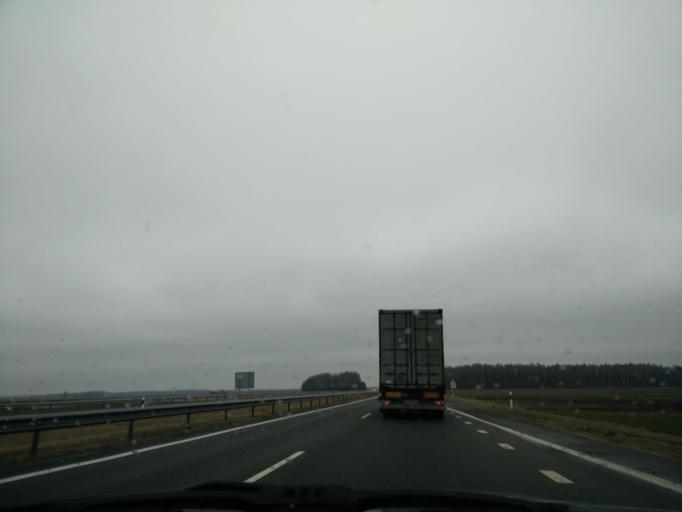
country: LT
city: Raseiniai
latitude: 55.3560
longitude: 23.0345
